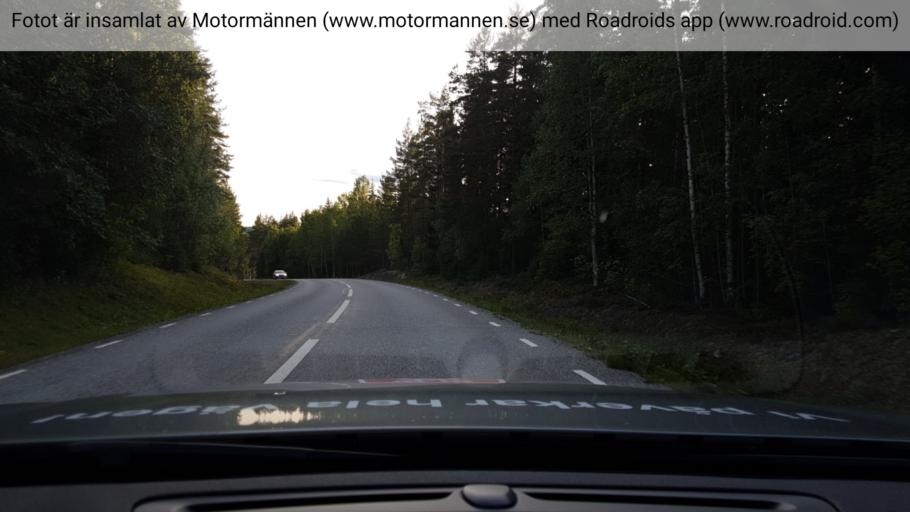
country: SE
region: OErebro
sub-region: Ljusnarsbergs Kommun
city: Kopparberg
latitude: 59.8796
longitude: 15.0584
